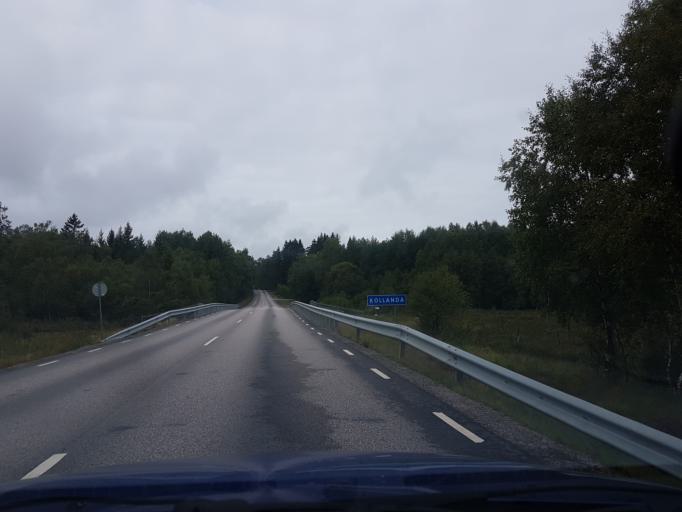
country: SE
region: Vaestra Goetaland
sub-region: Ale Kommun
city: Salanda
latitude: 57.9226
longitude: 12.2784
